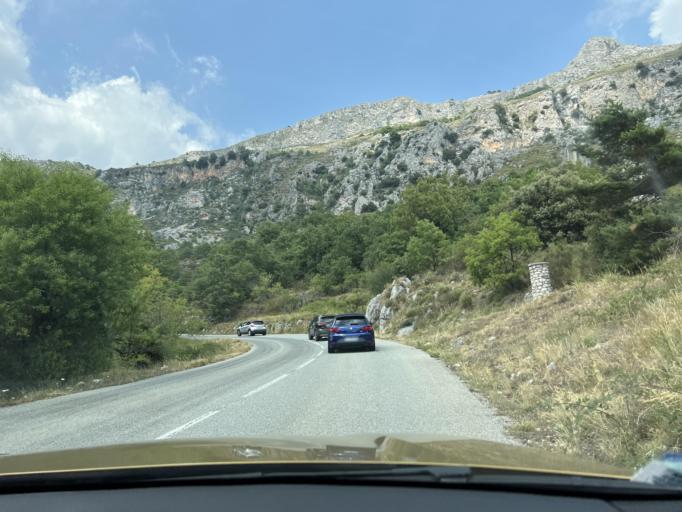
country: FR
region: Provence-Alpes-Cote d'Azur
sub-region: Departement des Alpes-Maritimes
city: Grasse
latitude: 43.7978
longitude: 6.9421
